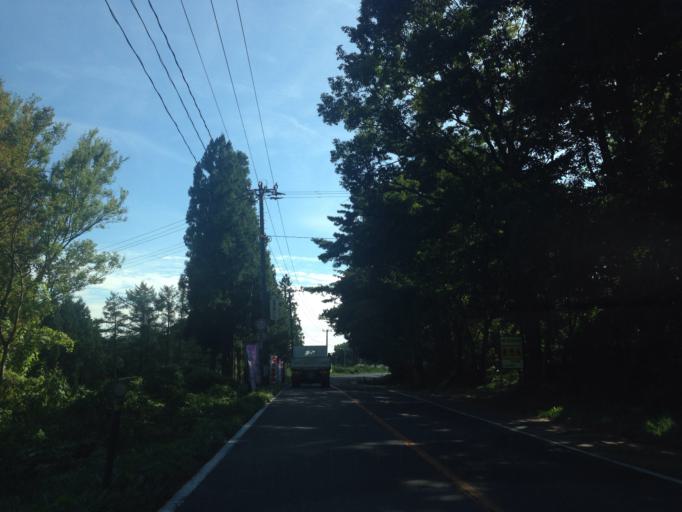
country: JP
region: Fukushima
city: Nihommatsu
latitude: 37.5823
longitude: 140.3528
